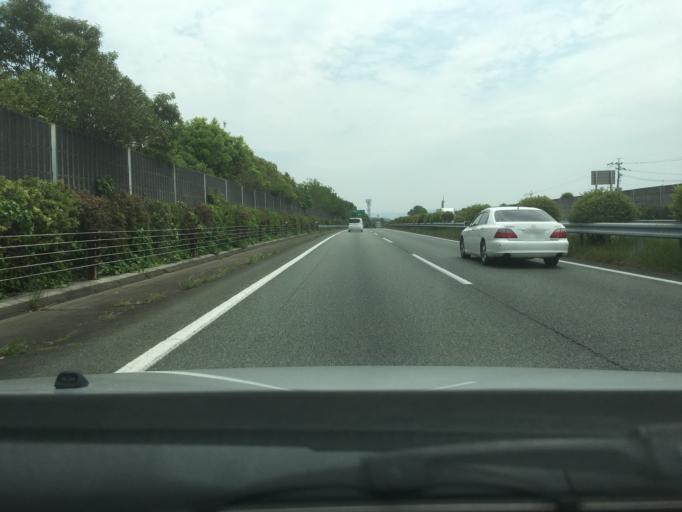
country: JP
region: Kumamoto
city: Kumamoto
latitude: 32.8529
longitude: 130.7618
